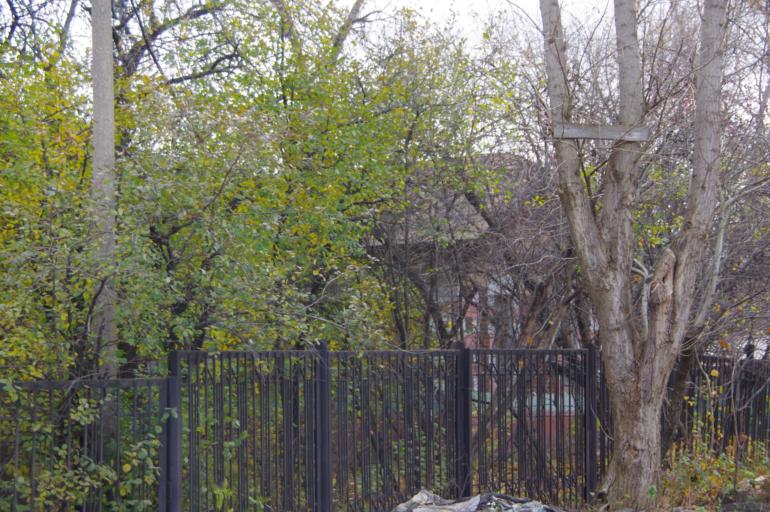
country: RU
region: Moscow
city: Novovladykino
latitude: 55.8481
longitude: 37.5977
